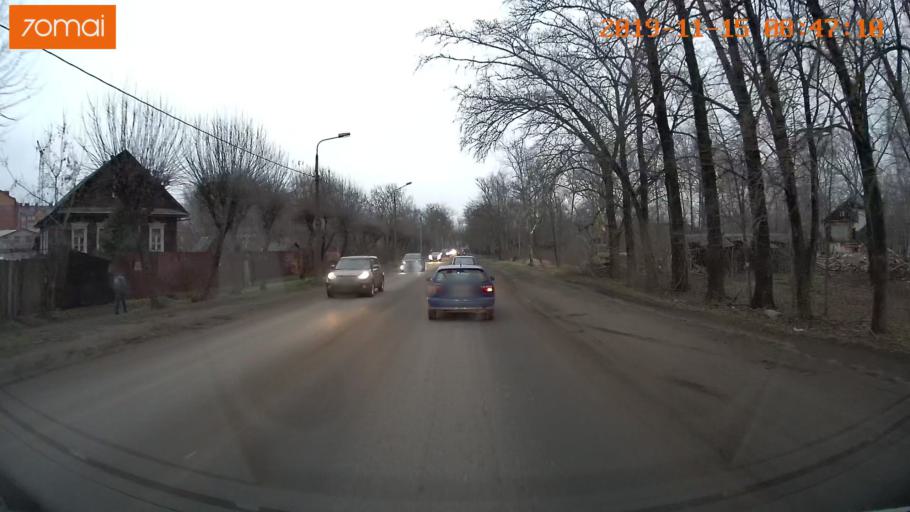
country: RU
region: Vologda
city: Cherepovets
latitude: 59.1201
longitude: 37.9129
